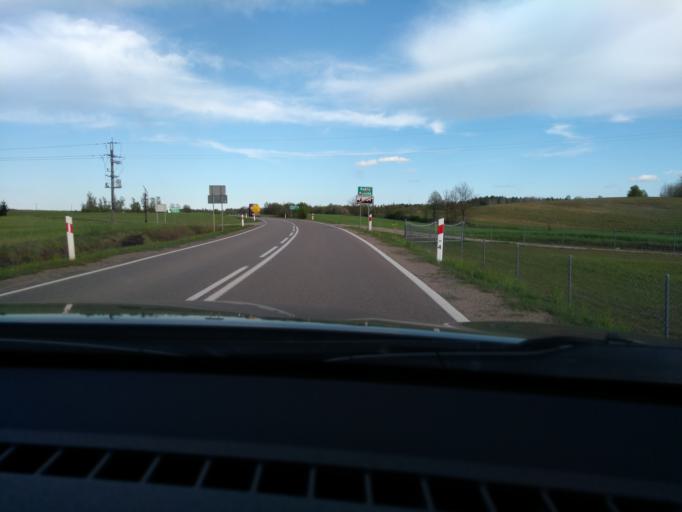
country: PL
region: Pomeranian Voivodeship
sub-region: Powiat leborski
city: Cewice
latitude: 54.3393
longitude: 17.6914
